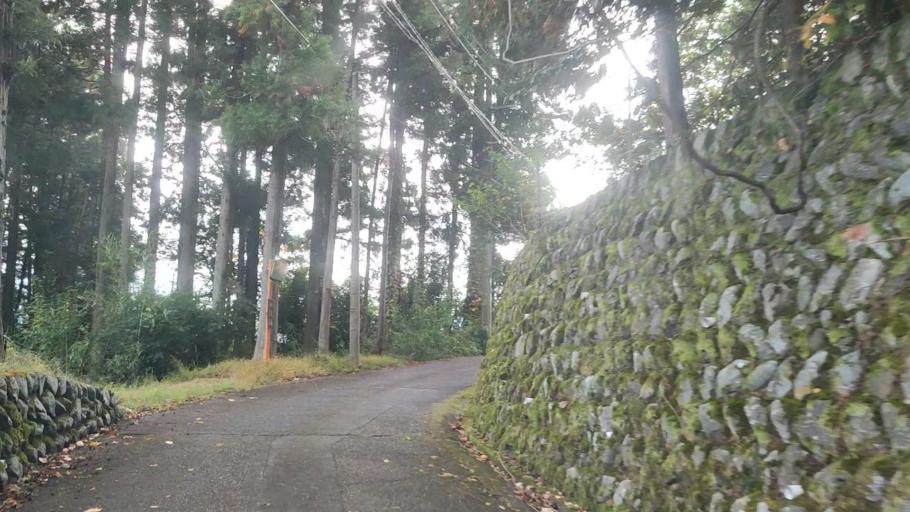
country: JP
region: Shizuoka
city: Fujinomiya
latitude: 35.3396
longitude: 138.4397
